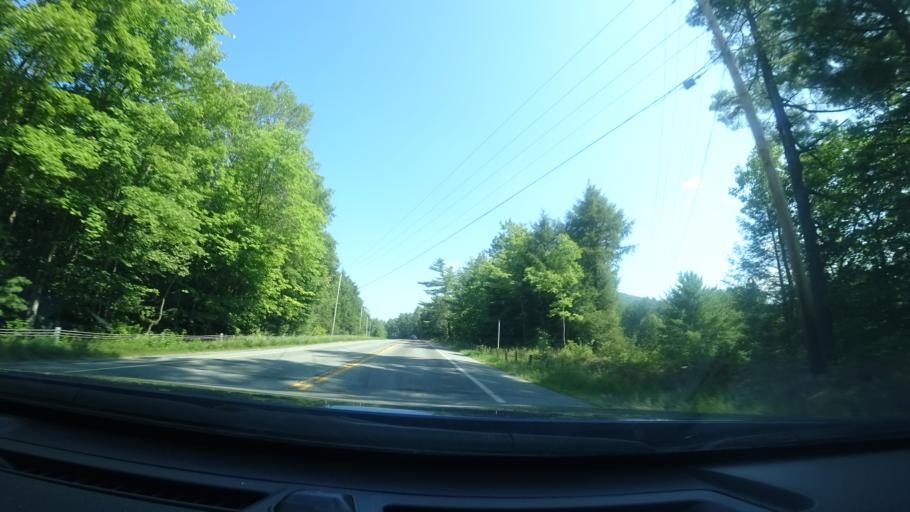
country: US
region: New York
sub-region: Warren County
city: Warrensburg
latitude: 43.6353
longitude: -73.7980
